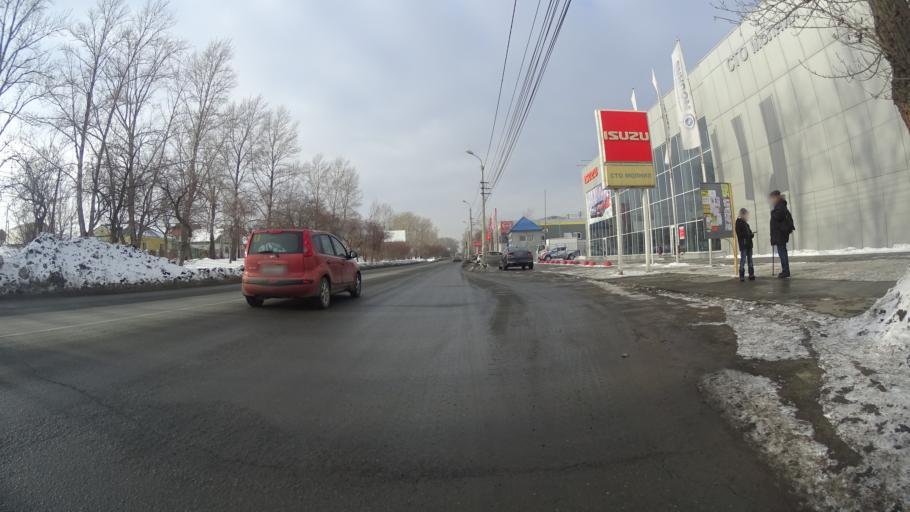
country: RU
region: Chelyabinsk
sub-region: Gorod Chelyabinsk
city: Chelyabinsk
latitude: 55.1190
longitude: 61.3830
